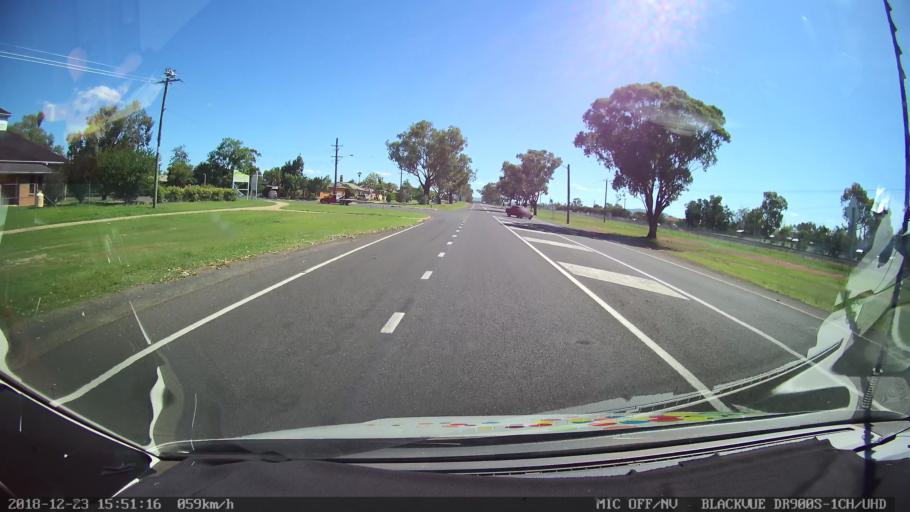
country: AU
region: New South Wales
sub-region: Tamworth Municipality
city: South Tamworth
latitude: -31.1115
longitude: 150.8969
